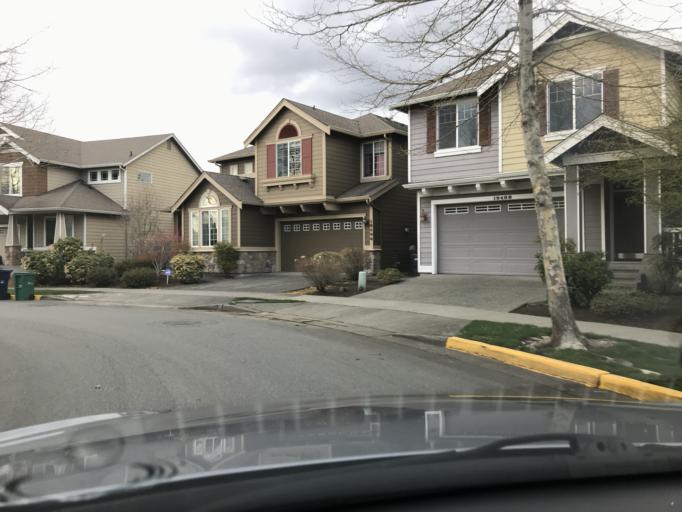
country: US
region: Washington
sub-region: King County
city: Sammamish
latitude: 47.6660
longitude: -122.0804
